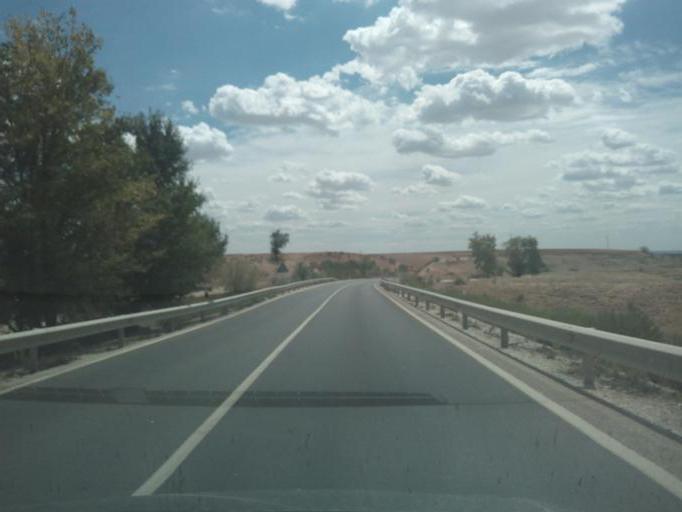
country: ES
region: Madrid
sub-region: Provincia de Madrid
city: Ajalvir
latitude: 40.5288
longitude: -3.4919
